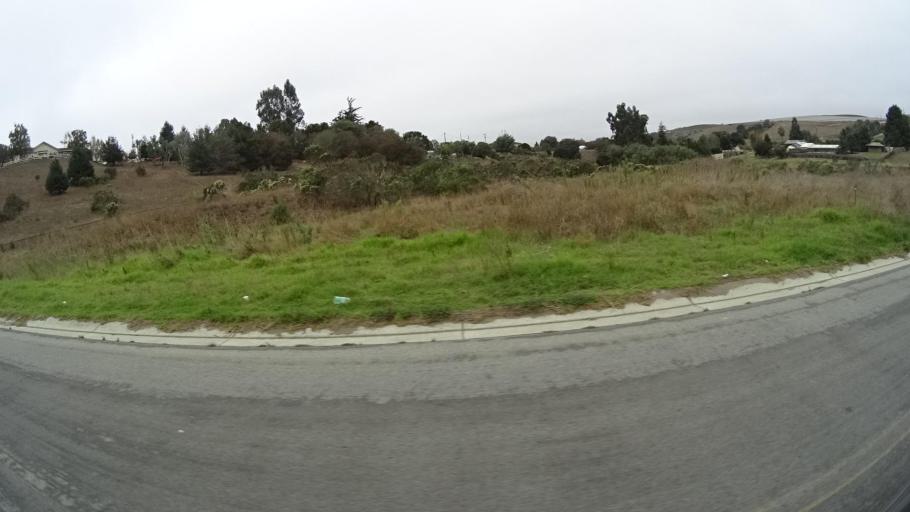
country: US
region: California
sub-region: Monterey County
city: Prunedale
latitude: 36.7659
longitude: -121.6647
